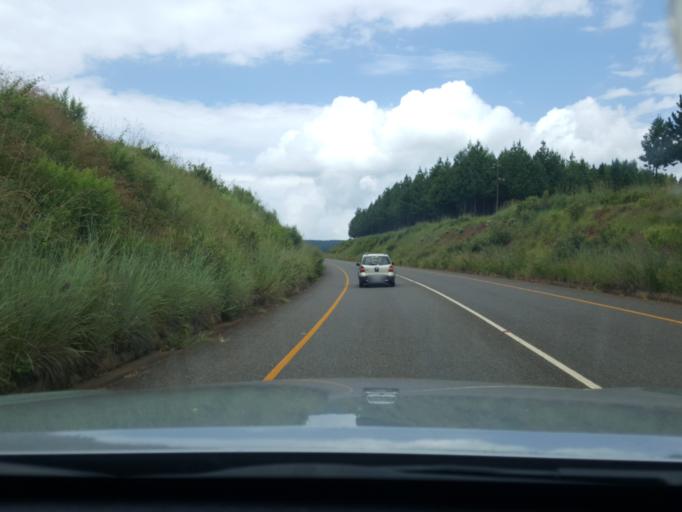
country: ZA
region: Mpumalanga
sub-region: Ehlanzeni District
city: Graksop
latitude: -25.1307
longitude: 30.8124
